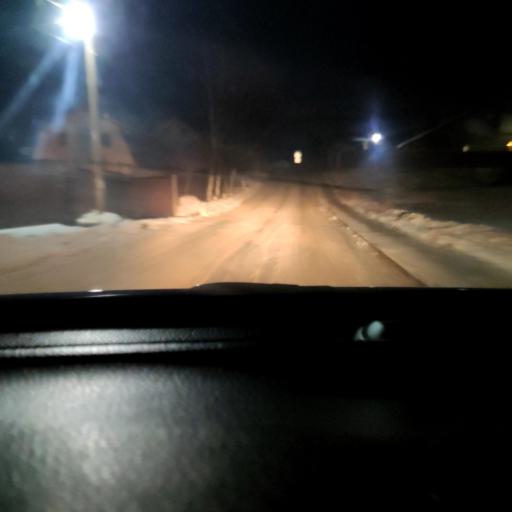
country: RU
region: Voronezj
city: Somovo
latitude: 51.6914
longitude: 39.3604
